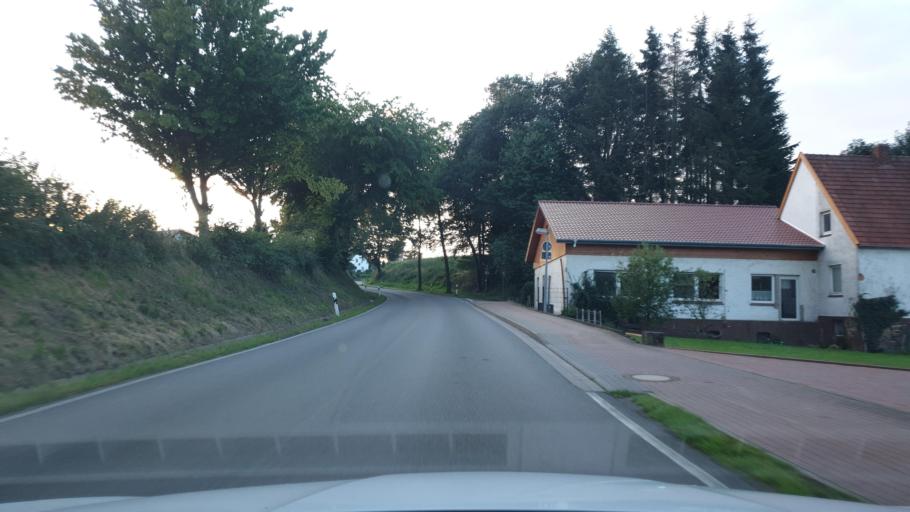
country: DE
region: North Rhine-Westphalia
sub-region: Regierungsbezirk Detmold
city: Huellhorst
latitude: 52.2582
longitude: 8.7265
